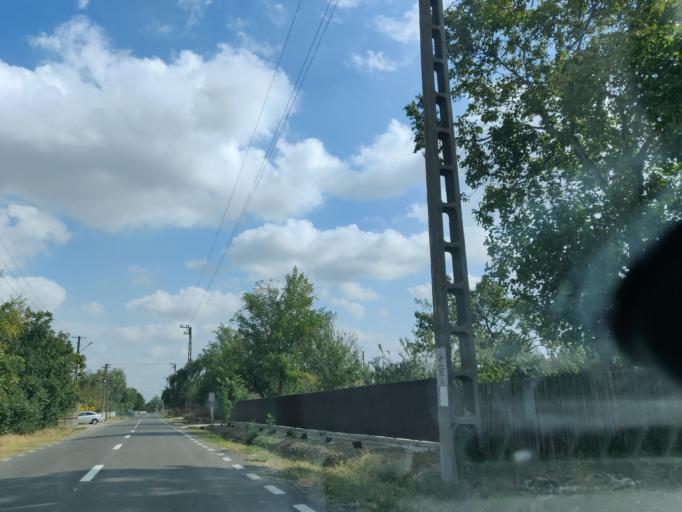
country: RO
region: Vrancea
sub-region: Comuna Ciorasti
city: Ciorasti
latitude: 45.4279
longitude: 27.2933
